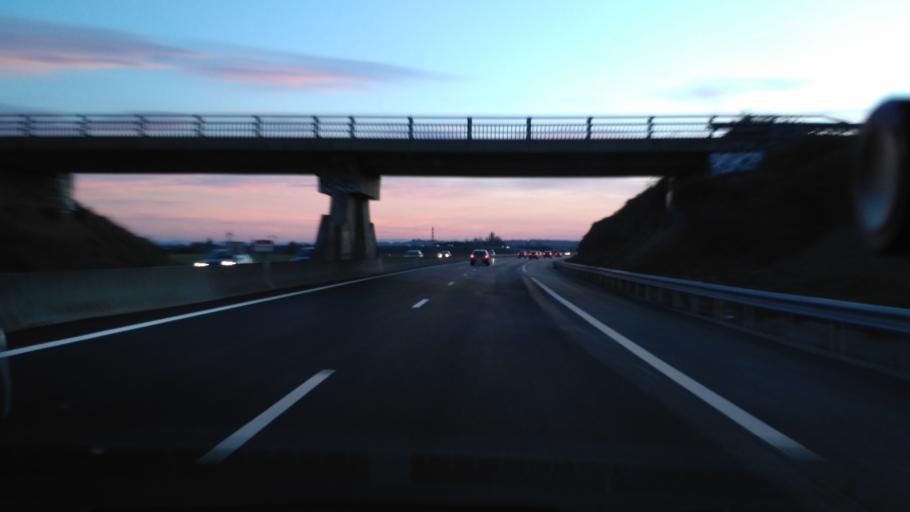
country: FR
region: Rhone-Alpes
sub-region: Departement de la Drome
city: Malissard
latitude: 44.9252
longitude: 4.9449
